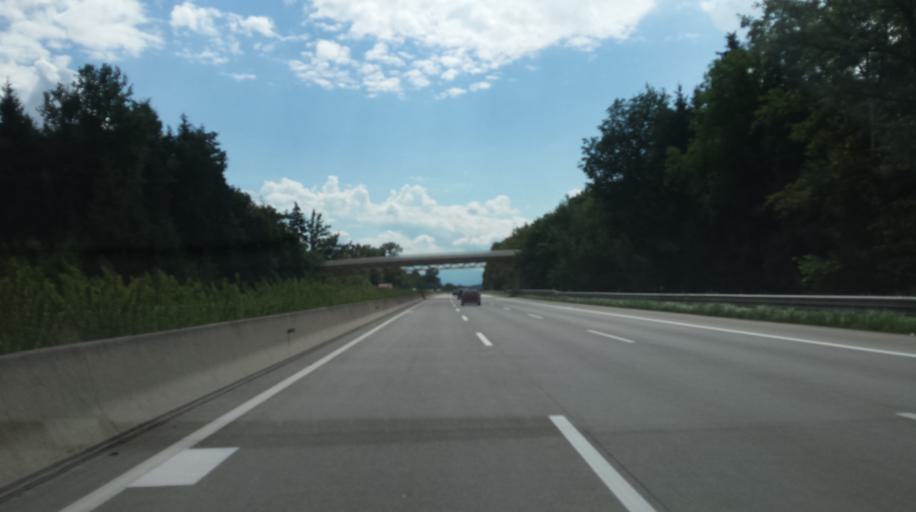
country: AT
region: Upper Austria
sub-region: Wels-Land
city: Sattledt
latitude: 48.1058
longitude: 14.0920
